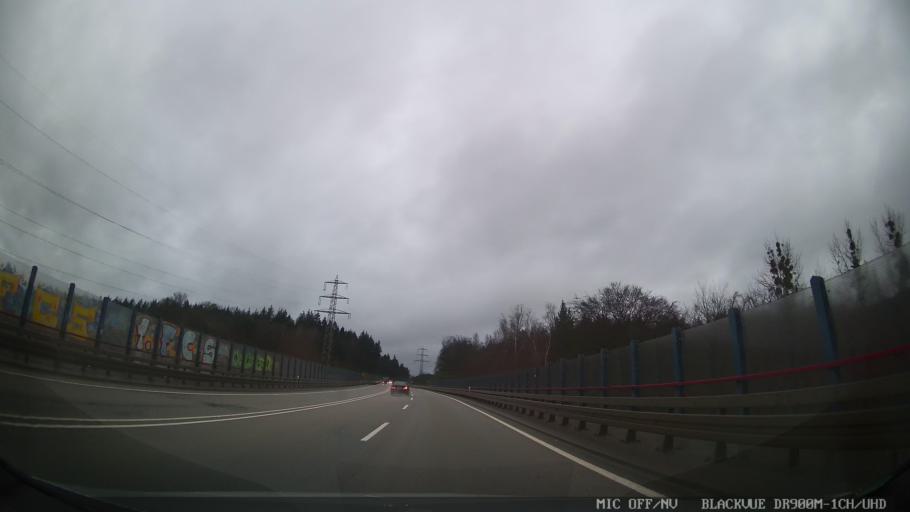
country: DE
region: Saarland
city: Merzig
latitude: 49.4769
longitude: 6.6281
